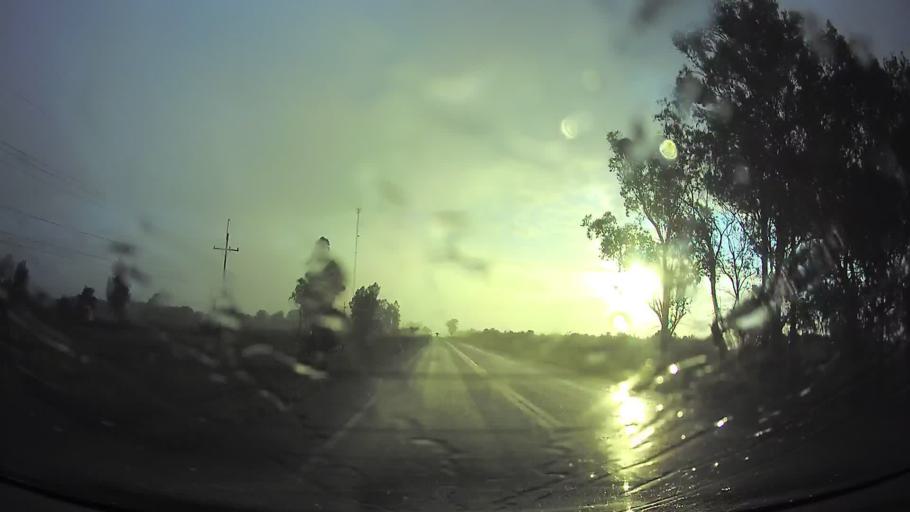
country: PY
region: Paraguari
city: Paraguari
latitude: -25.6942
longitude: -57.1709
